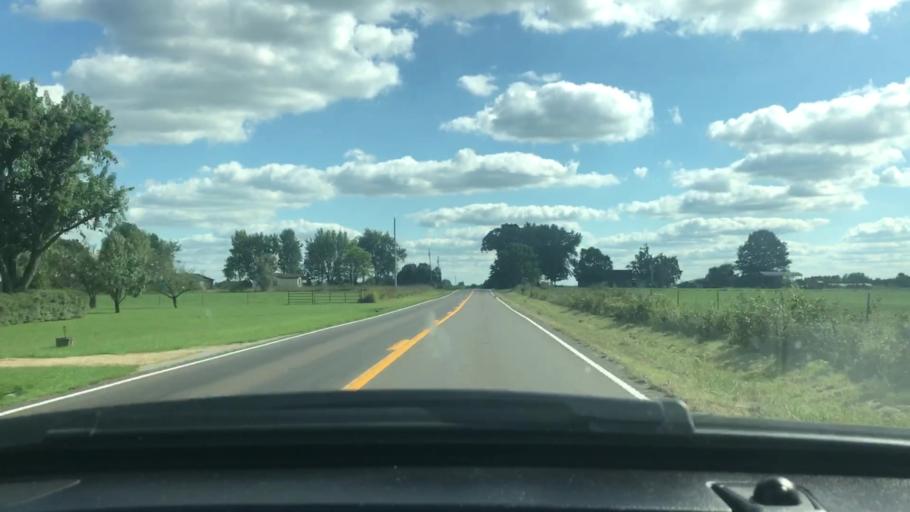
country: US
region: Missouri
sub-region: Wright County
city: Mountain Grove
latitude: 37.2644
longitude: -92.3081
